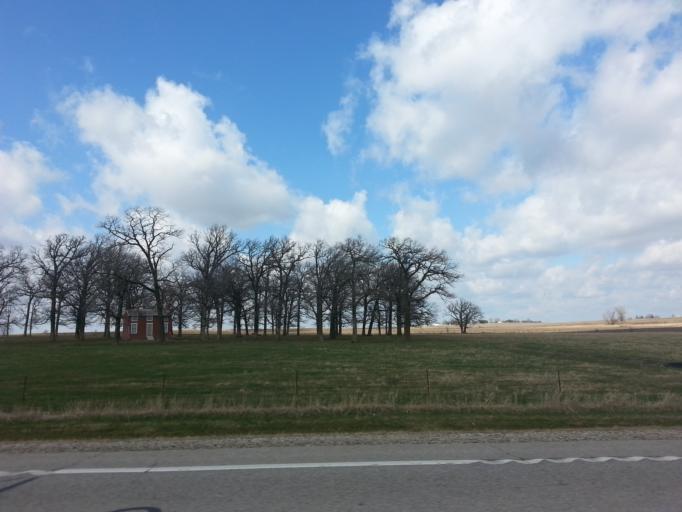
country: US
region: Minnesota
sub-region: Dodge County
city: Mantorville
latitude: 44.0803
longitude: -92.8084
